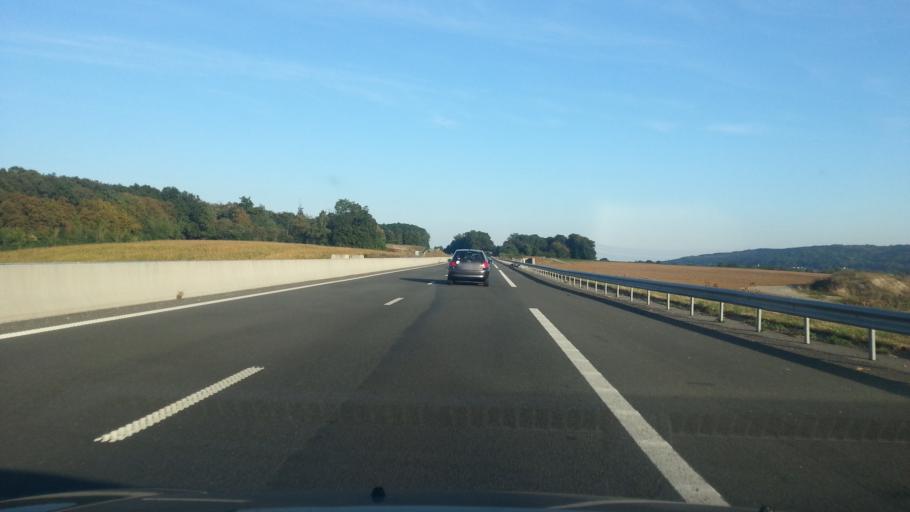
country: FR
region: Picardie
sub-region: Departement de l'Oise
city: Breuil-le-Sec
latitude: 49.3856
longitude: 2.4708
